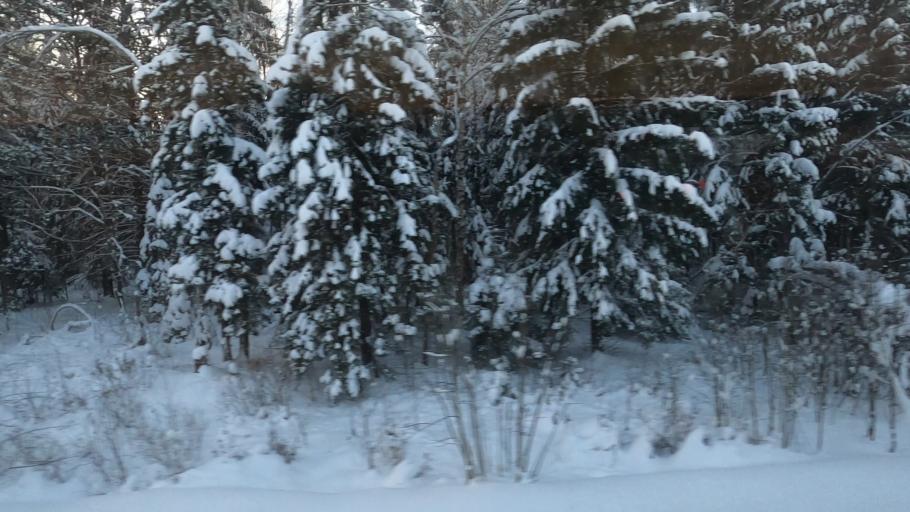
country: RU
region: Moskovskaya
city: Novo-Nikol'skoye
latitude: 56.6017
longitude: 37.5673
